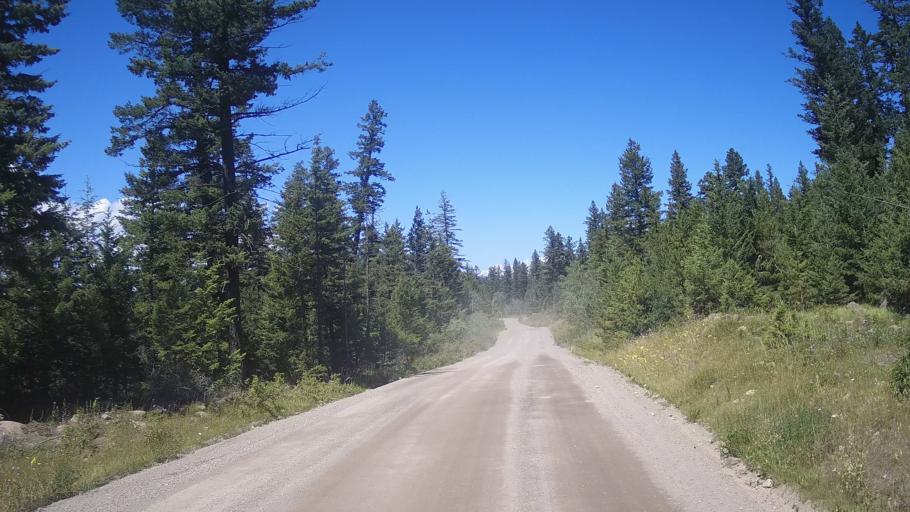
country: CA
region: British Columbia
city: Cache Creek
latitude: 51.1556
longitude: -121.5490
